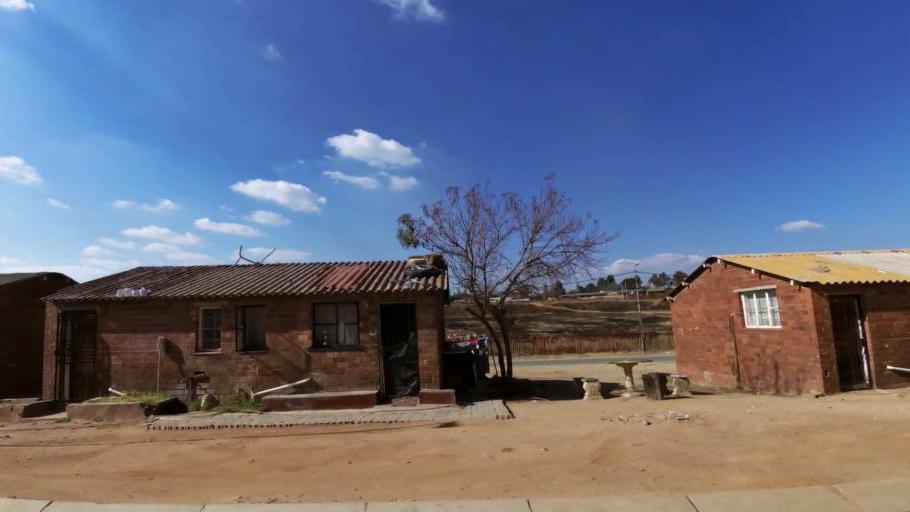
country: ZA
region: Gauteng
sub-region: City of Johannesburg Metropolitan Municipality
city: Soweto
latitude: -26.2254
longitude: 27.9246
